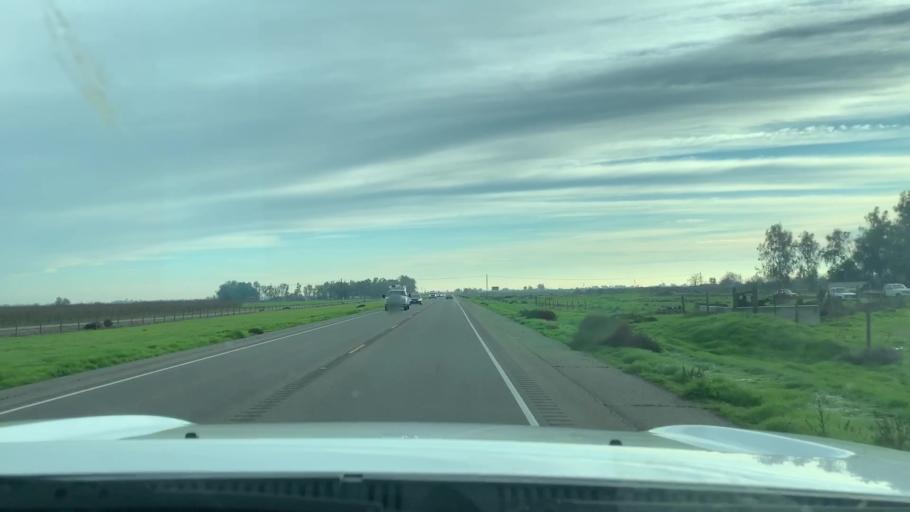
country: US
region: California
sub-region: Fresno County
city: Riverdale
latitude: 36.4697
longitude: -119.7942
